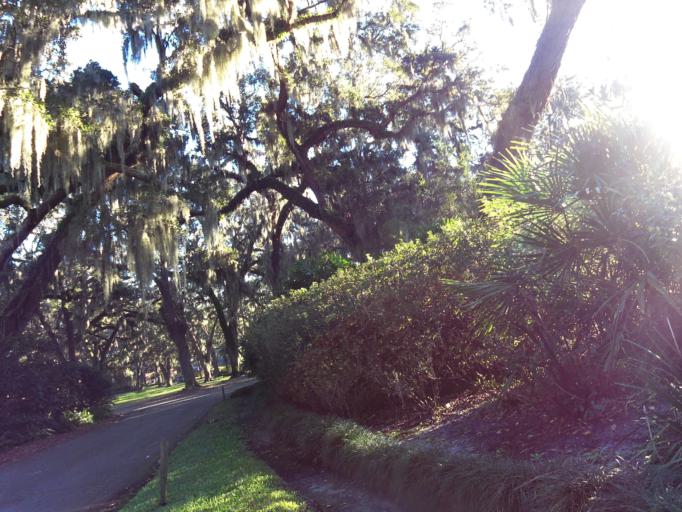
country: US
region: Florida
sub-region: Duval County
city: Jacksonville
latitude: 30.2798
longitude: -81.7001
